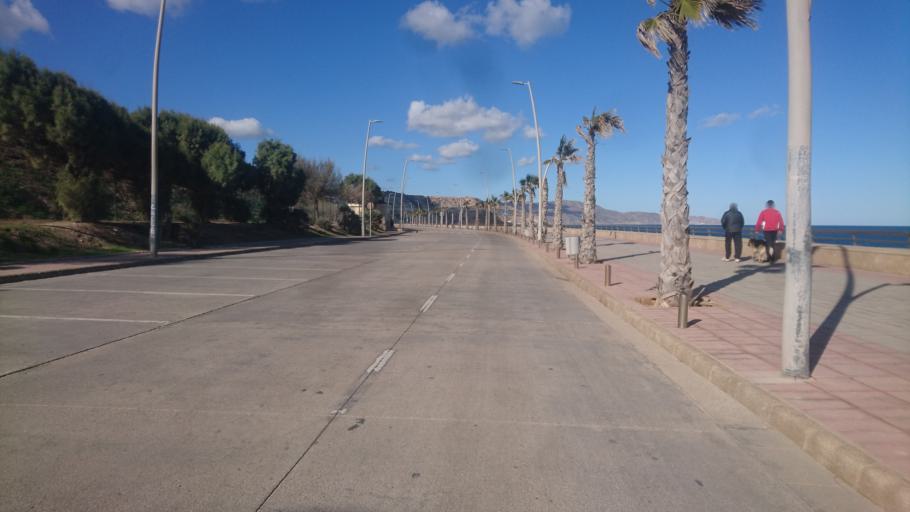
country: ES
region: Melilla
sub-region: Melilla
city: Melilla
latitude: 35.3014
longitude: -2.9372
